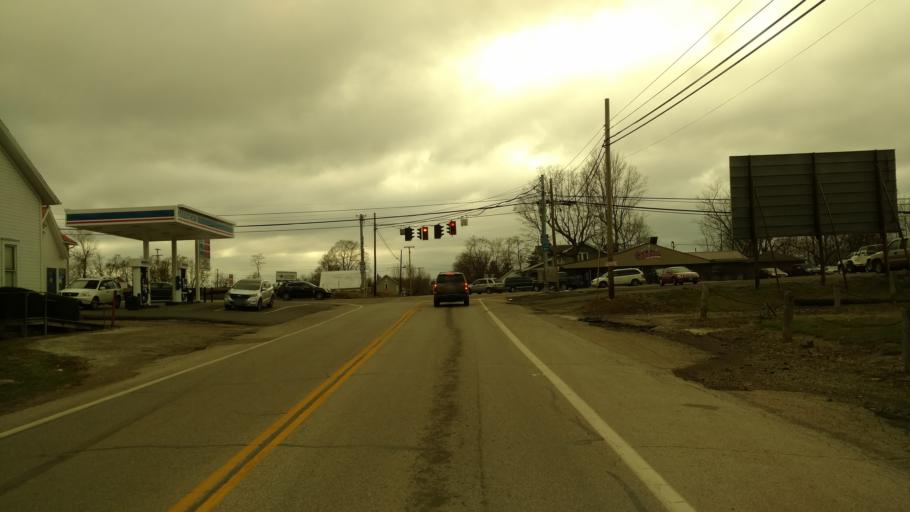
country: US
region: Ohio
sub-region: Licking County
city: Harbor Hills
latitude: 39.9594
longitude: -82.4132
